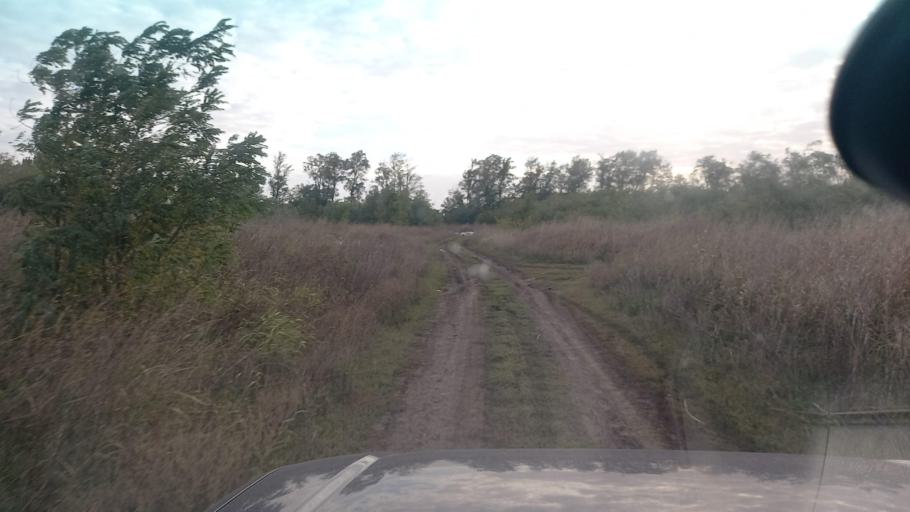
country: RU
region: Krasnodarskiy
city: Krasnodar
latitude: 45.1276
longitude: 38.9159
